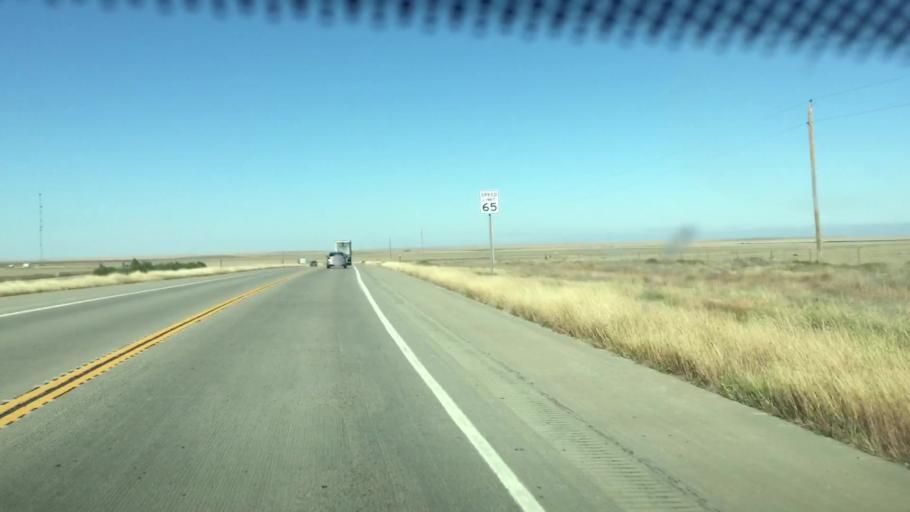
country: US
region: Colorado
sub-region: Prowers County
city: Lamar
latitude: 38.2700
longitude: -102.7225
